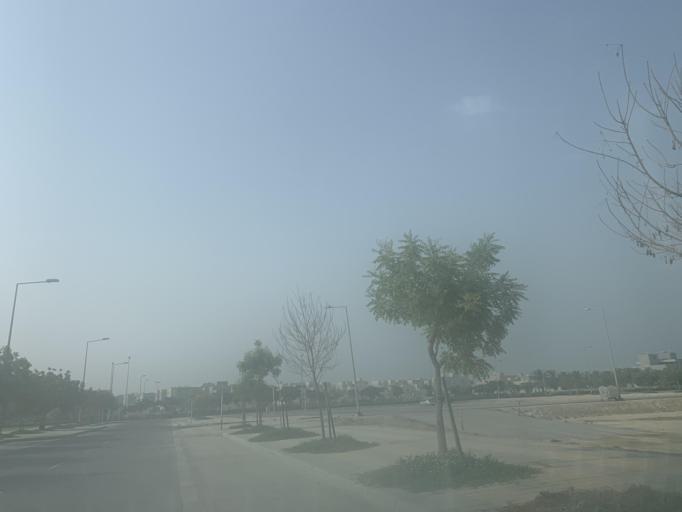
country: BH
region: Manama
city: Jidd Hafs
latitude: 26.2302
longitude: 50.4520
